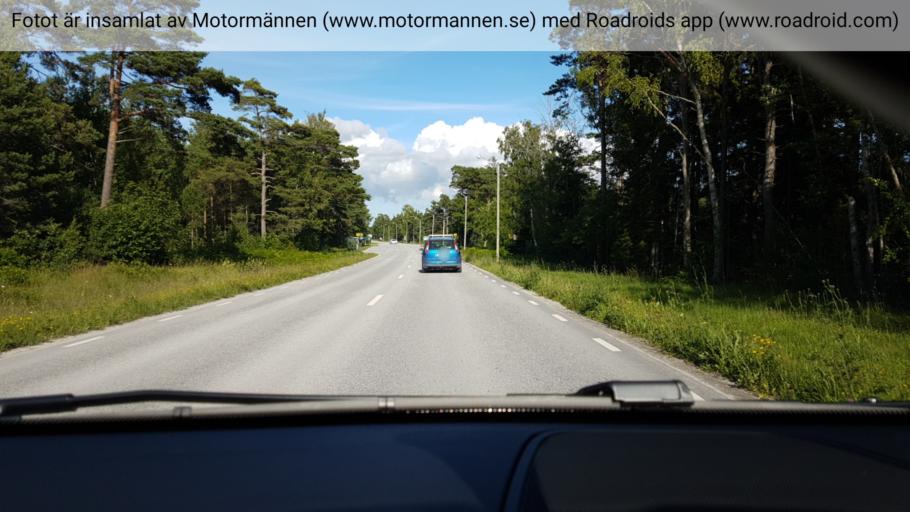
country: SE
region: Gotland
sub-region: Gotland
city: Slite
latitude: 57.7498
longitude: 18.7263
